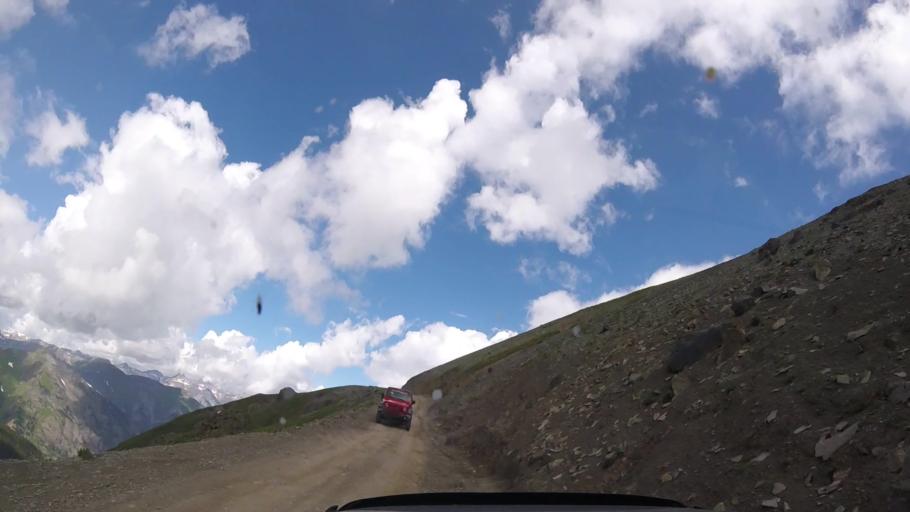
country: US
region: Colorado
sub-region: Ouray County
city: Ouray
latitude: 37.9677
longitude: -107.5885
